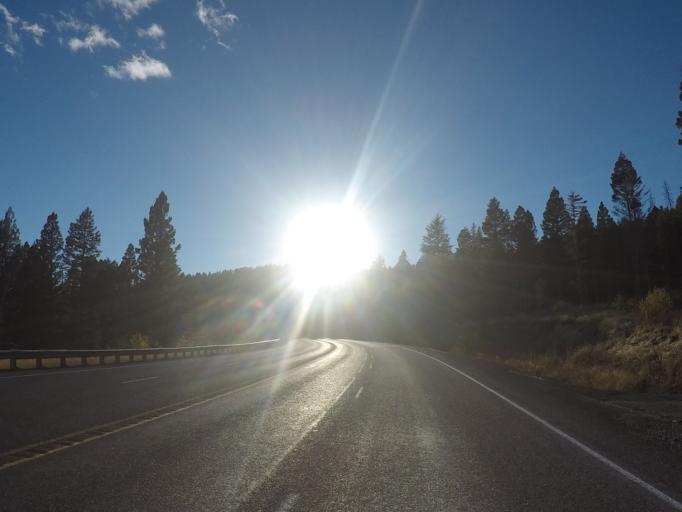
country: US
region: Montana
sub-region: Lewis and Clark County
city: Helena West Side
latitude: 46.5747
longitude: -112.2962
